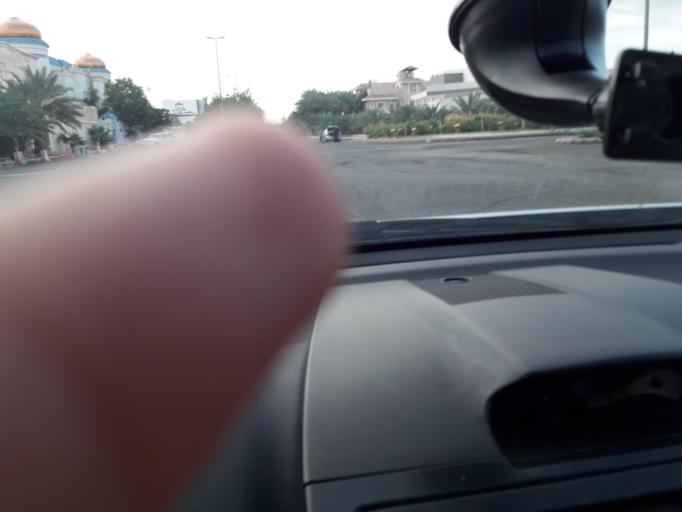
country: SA
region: Al Madinah al Munawwarah
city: Medina
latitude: 24.4244
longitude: 39.6271
